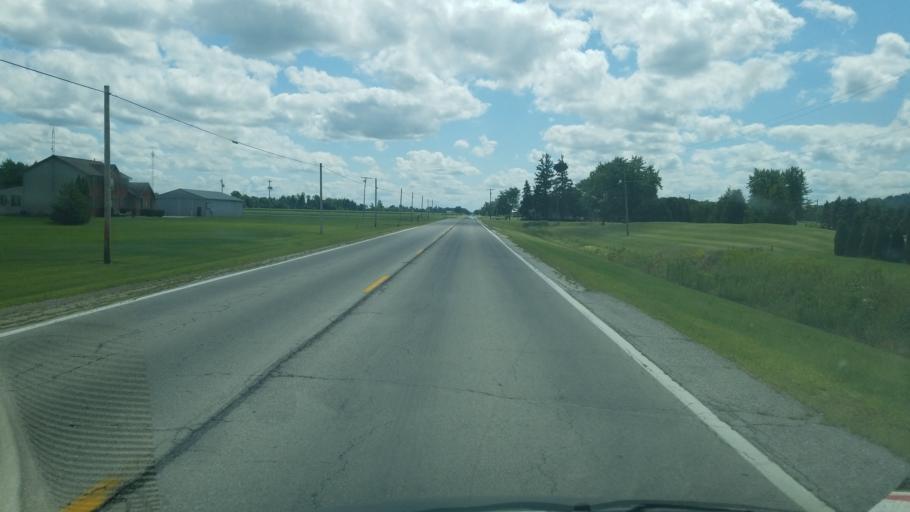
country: US
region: Ohio
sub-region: Henry County
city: Napoleon
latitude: 41.3282
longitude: -84.1187
